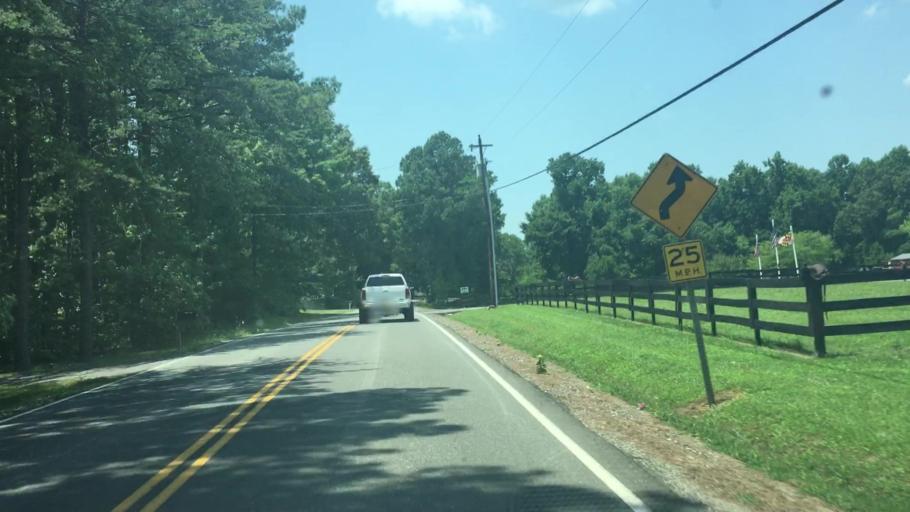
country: US
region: Maryland
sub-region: Saint Mary's County
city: Mechanicsville
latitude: 38.3740
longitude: -76.6888
